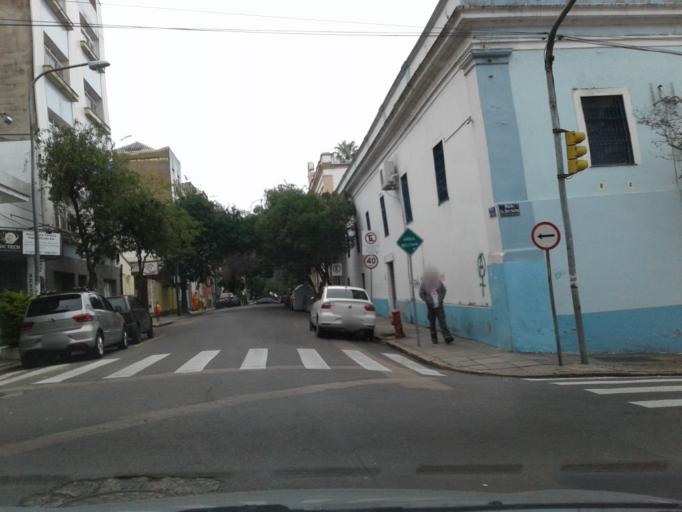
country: BR
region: Rio Grande do Sul
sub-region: Porto Alegre
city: Porto Alegre
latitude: -30.0328
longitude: -51.2346
